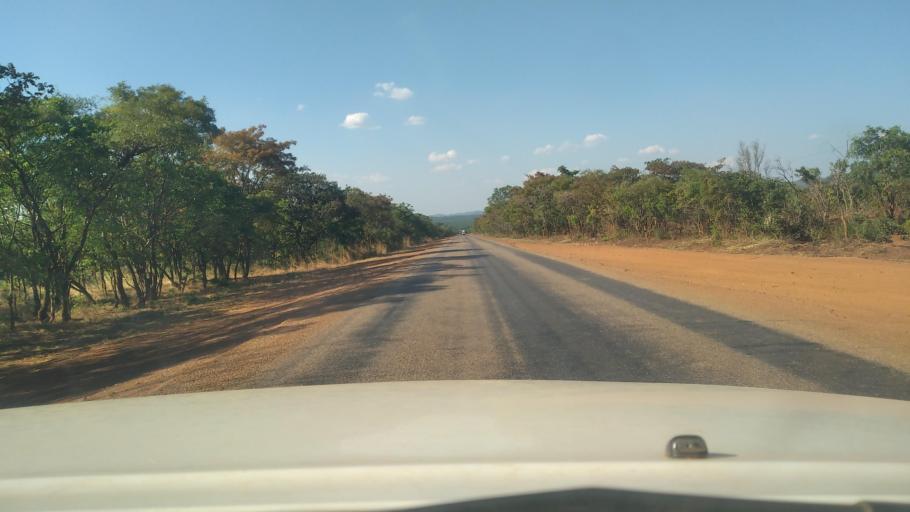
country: ZM
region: Northern
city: Mpika
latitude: -11.7602
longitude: 31.4632
